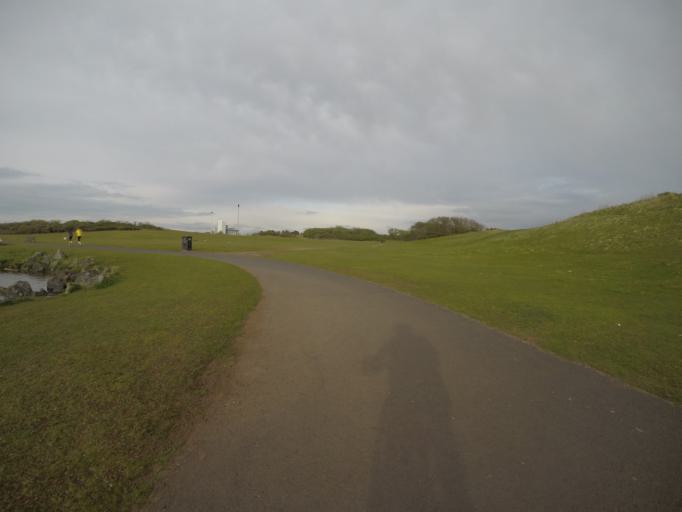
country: GB
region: Scotland
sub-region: North Ayrshire
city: Irvine
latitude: 55.6038
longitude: -4.6863
